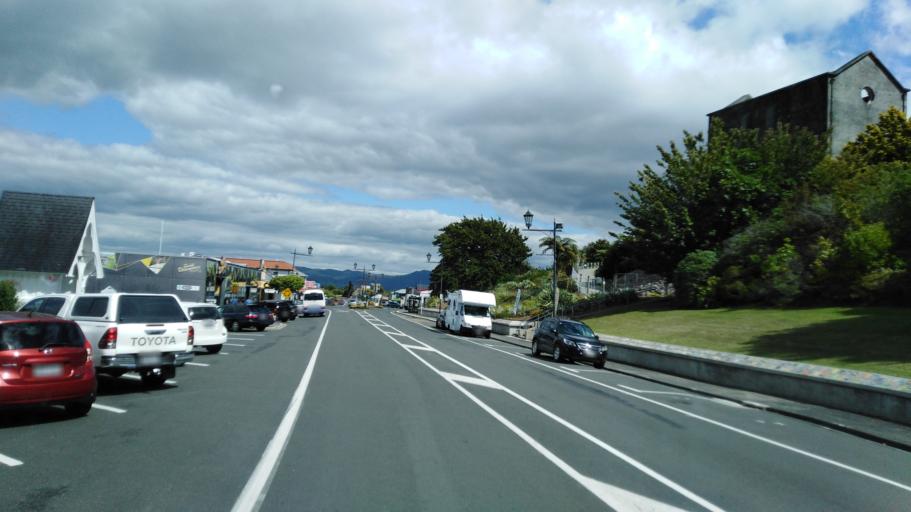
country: NZ
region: Waikato
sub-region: Hauraki District
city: Waihi
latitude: -37.3894
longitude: 175.8442
